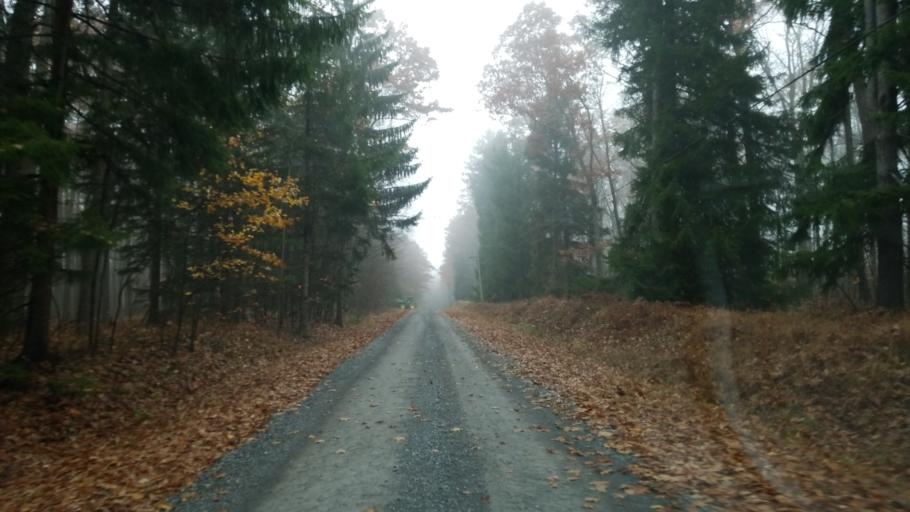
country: US
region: Pennsylvania
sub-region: Clearfield County
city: Clearfield
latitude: 41.1040
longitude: -78.5263
